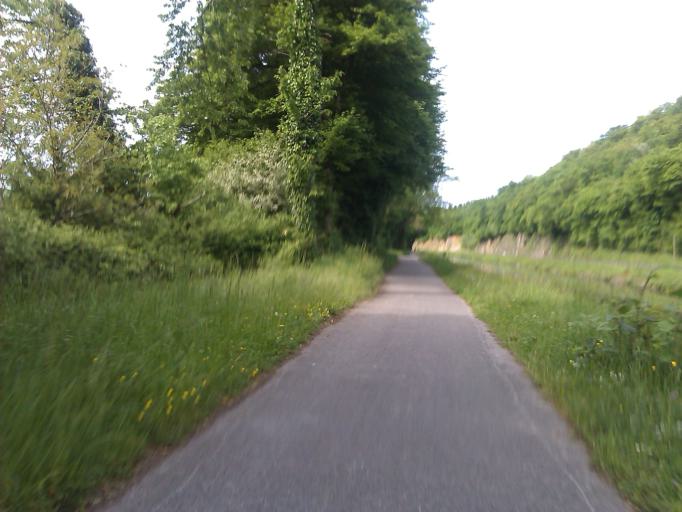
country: FR
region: Franche-Comte
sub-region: Departement du Doubs
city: Boussieres
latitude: 47.1504
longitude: 5.8546
